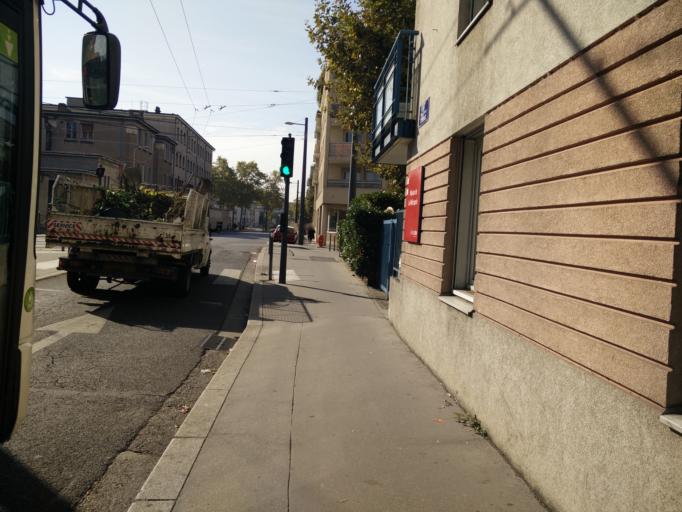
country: FR
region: Rhone-Alpes
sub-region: Departement du Rhone
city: Villeurbanne
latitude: 45.7450
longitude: 4.8792
